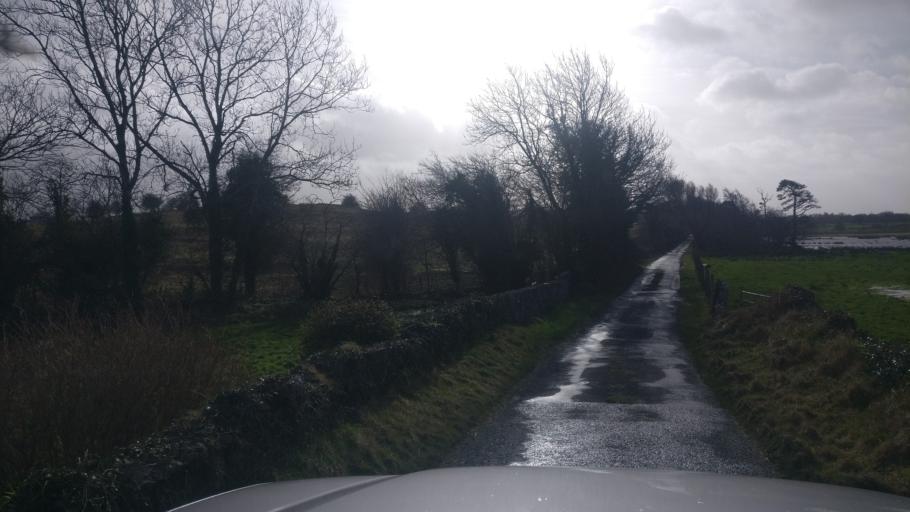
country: IE
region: Connaught
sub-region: County Galway
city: Loughrea
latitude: 53.2816
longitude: -8.5962
